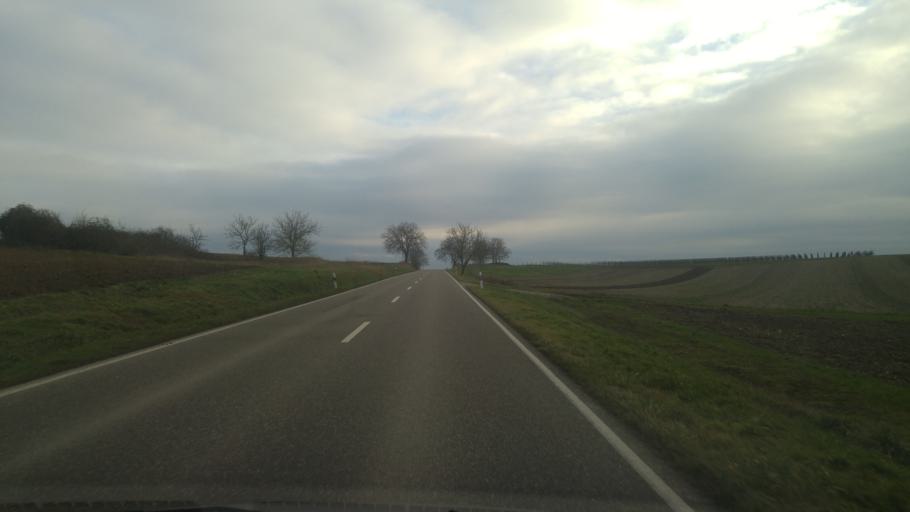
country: DE
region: Rheinland-Pfalz
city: Winden
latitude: 49.0818
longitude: 8.1281
